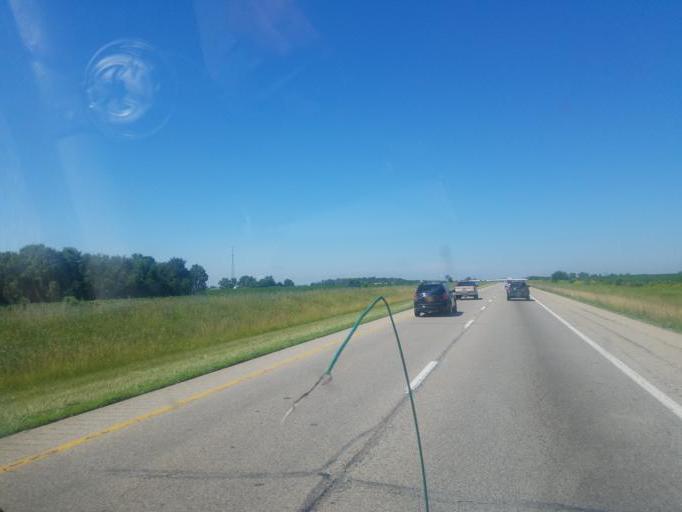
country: US
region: Ohio
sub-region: Clinton County
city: Wilmington
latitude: 39.4912
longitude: -83.9269
